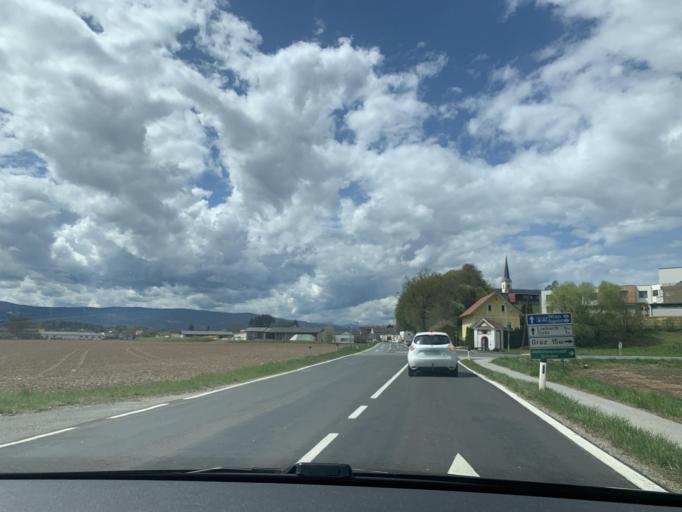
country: AT
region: Styria
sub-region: Politischer Bezirk Graz-Umgebung
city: Unterpremstatten
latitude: 46.9455
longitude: 15.3828
